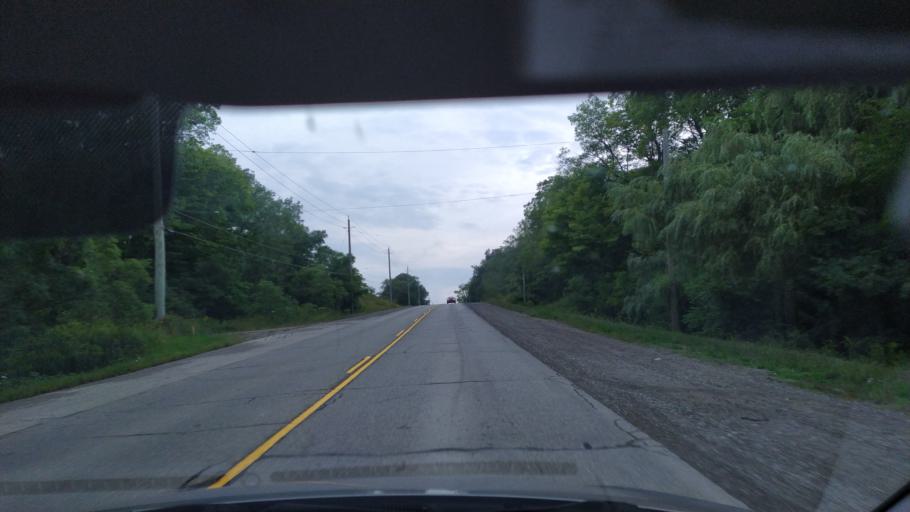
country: CA
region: Ontario
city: Cambridge
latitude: 43.3463
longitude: -80.3603
